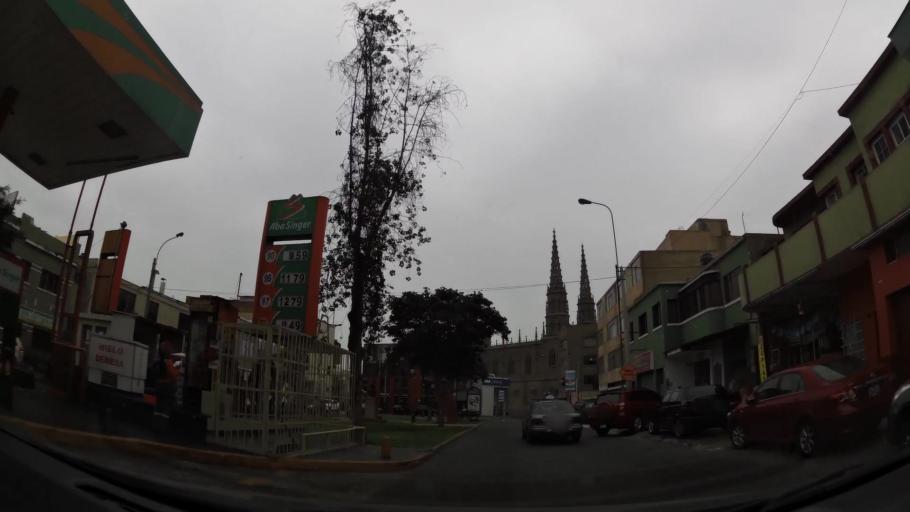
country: PE
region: Lima
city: Lima
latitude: -12.0750
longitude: -77.0470
